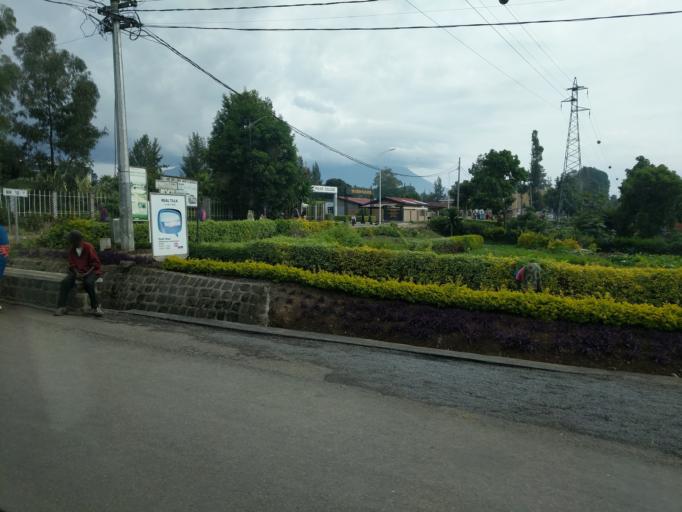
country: RW
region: Northern Province
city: Musanze
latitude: -1.5085
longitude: 29.6394
